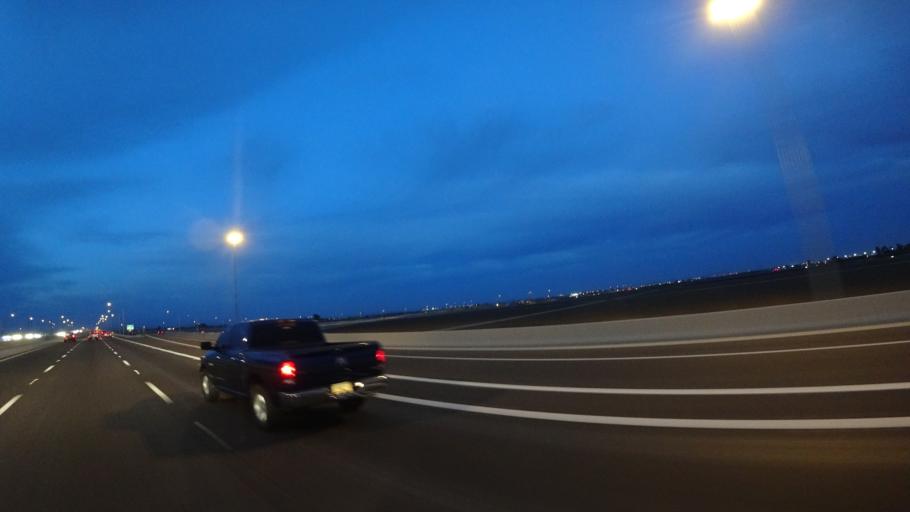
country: US
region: Arizona
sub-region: Maricopa County
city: Citrus Park
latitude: 33.5543
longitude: -112.4181
